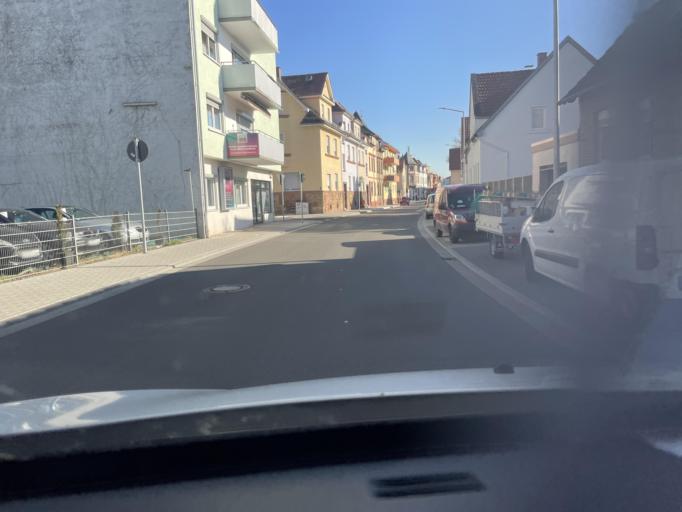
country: DE
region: Rheinland-Pfalz
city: Worms
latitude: 49.6458
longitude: 8.3498
